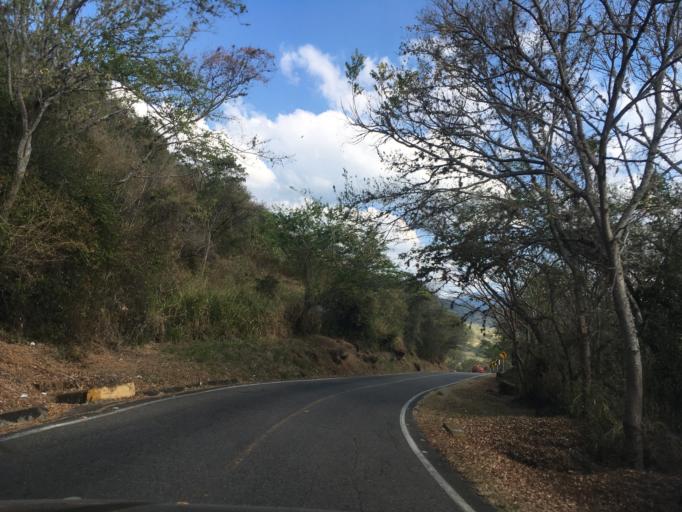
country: CO
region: Santander
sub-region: San Gil
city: San Gil
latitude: 6.5718
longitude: -73.1408
